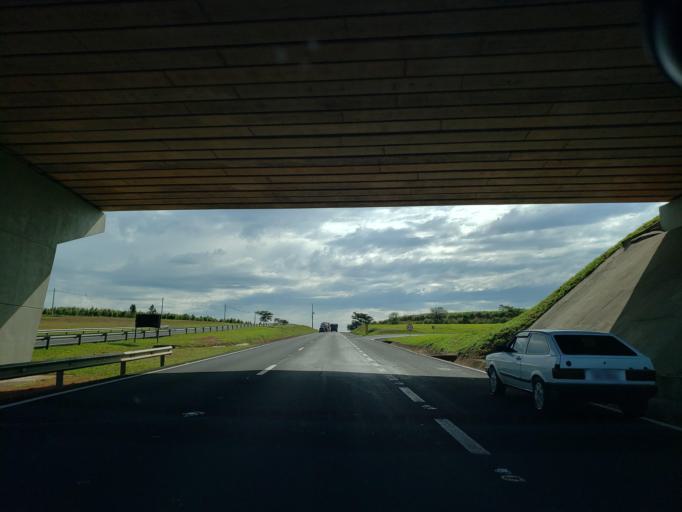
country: BR
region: Sao Paulo
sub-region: Cafelandia
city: Cafelandia
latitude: -21.8747
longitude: -49.5610
